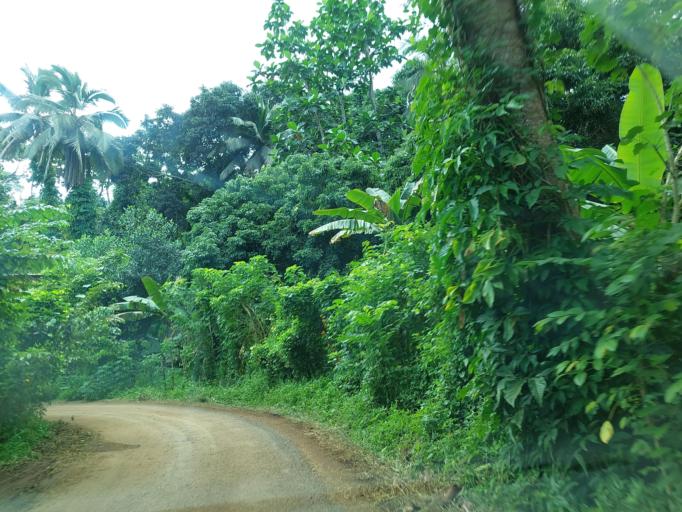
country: YT
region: Tsingoni
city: Tsingoni
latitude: -12.7731
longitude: 45.1121
